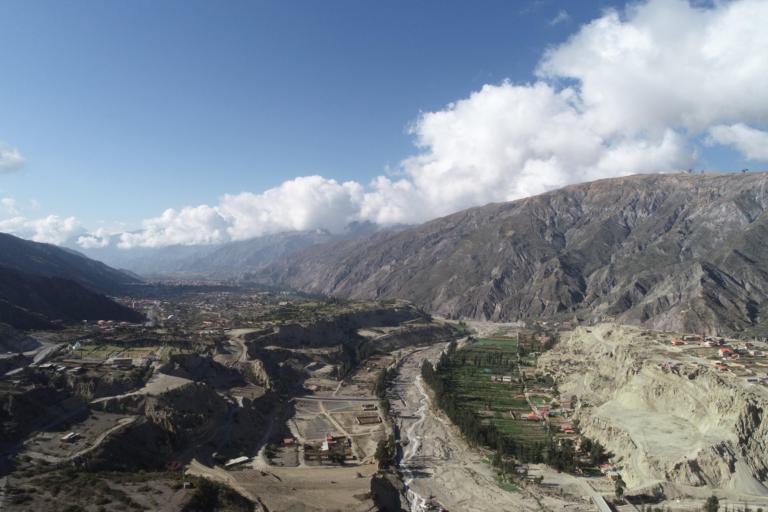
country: BO
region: La Paz
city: La Paz
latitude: -16.6125
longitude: -68.0628
